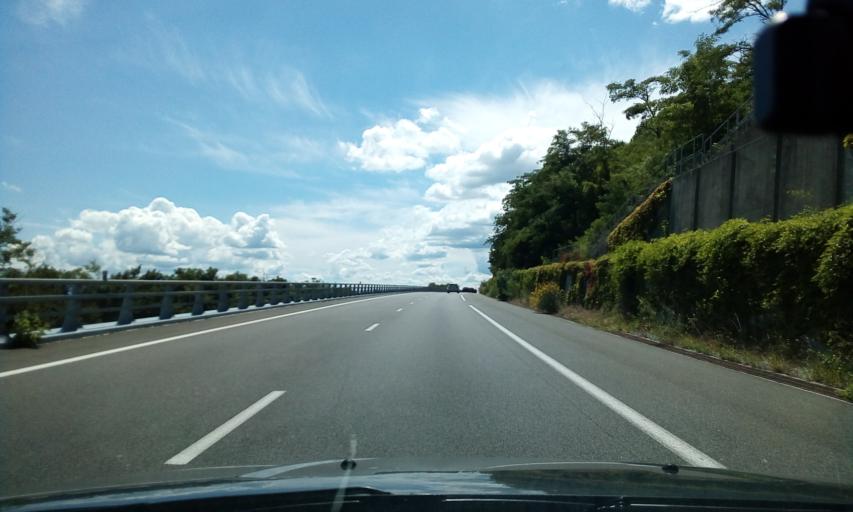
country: FR
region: Rhone-Alpes
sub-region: Departement de l'Isere
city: Saint-Sauveur
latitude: 45.1673
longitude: 5.3752
